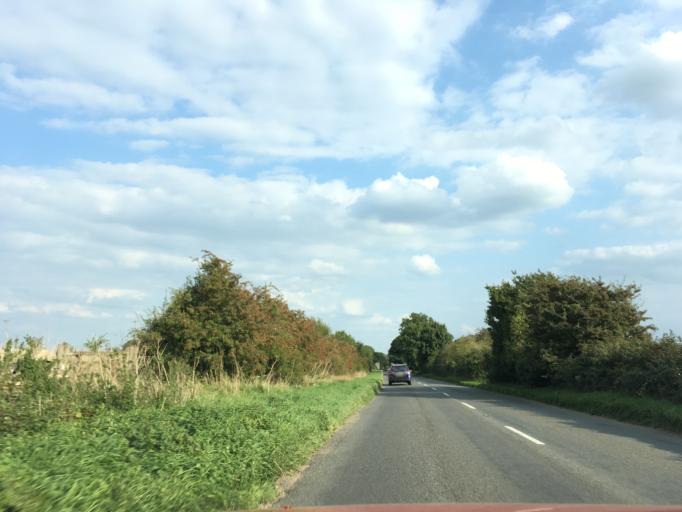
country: GB
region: England
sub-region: Gloucestershire
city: Nailsworth
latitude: 51.6510
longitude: -2.2300
